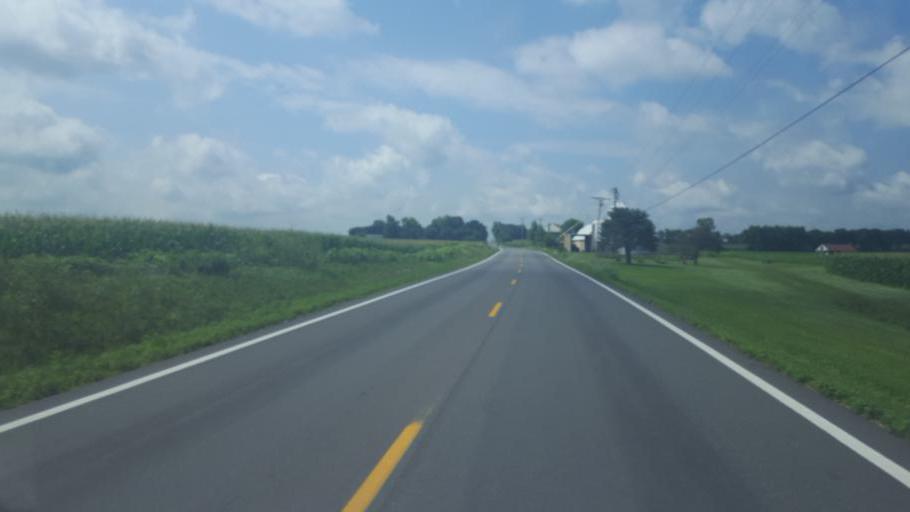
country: US
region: Ohio
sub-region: Fairfield County
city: Millersport
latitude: 39.9097
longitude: -82.5581
